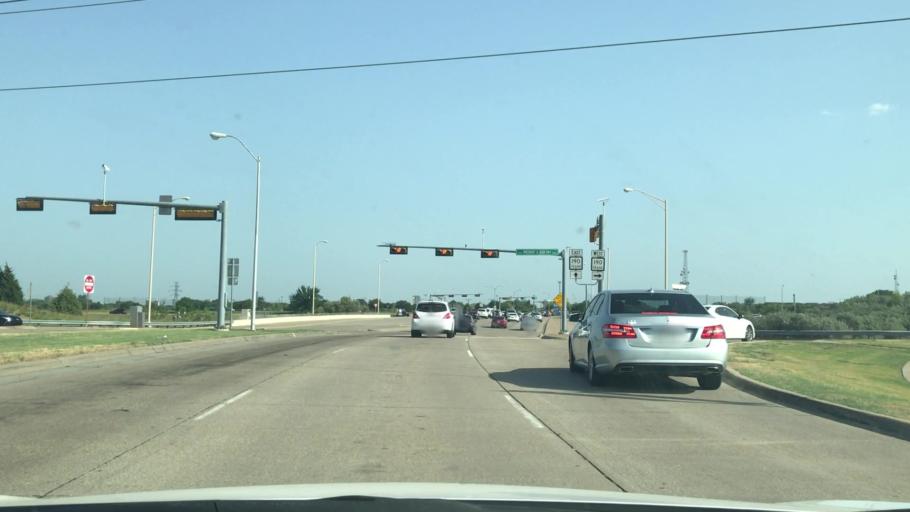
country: US
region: Texas
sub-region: Collin County
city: Plano
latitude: 33.0047
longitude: -96.7489
